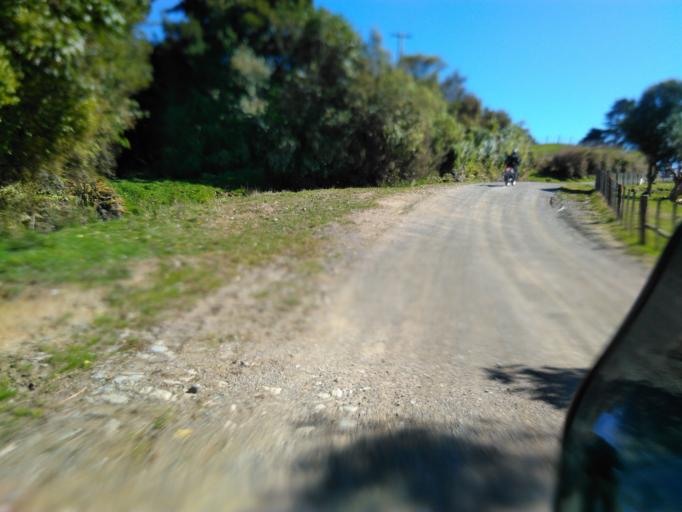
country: NZ
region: Bay of Plenty
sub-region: Opotiki District
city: Opotiki
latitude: -38.3560
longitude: 177.5897
